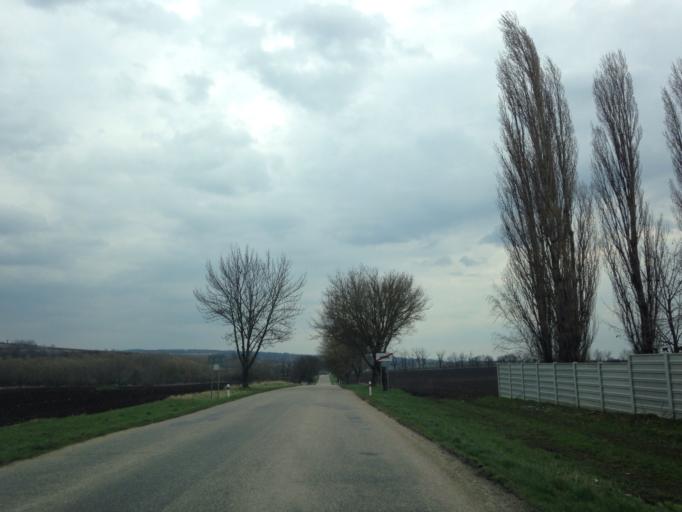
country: SK
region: Nitriansky
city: Svodin
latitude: 47.9810
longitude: 18.4026
